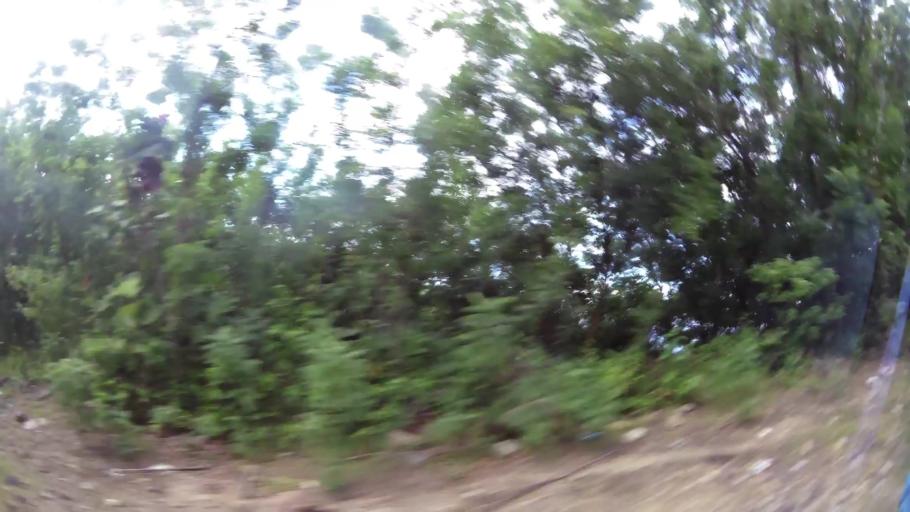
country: MS
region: Saint Peter
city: Brades
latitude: 16.7721
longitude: -62.1715
